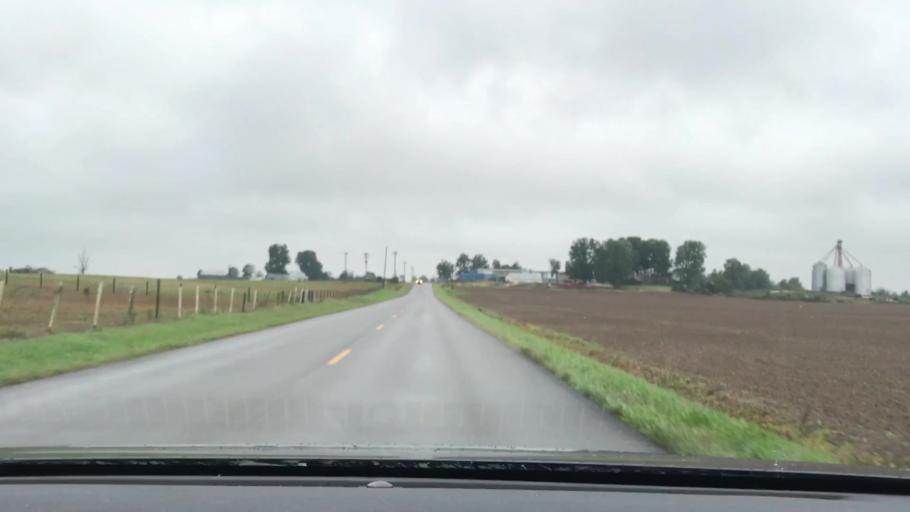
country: US
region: Kentucky
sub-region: Hopkins County
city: Madisonville
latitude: 37.3751
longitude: -87.3494
